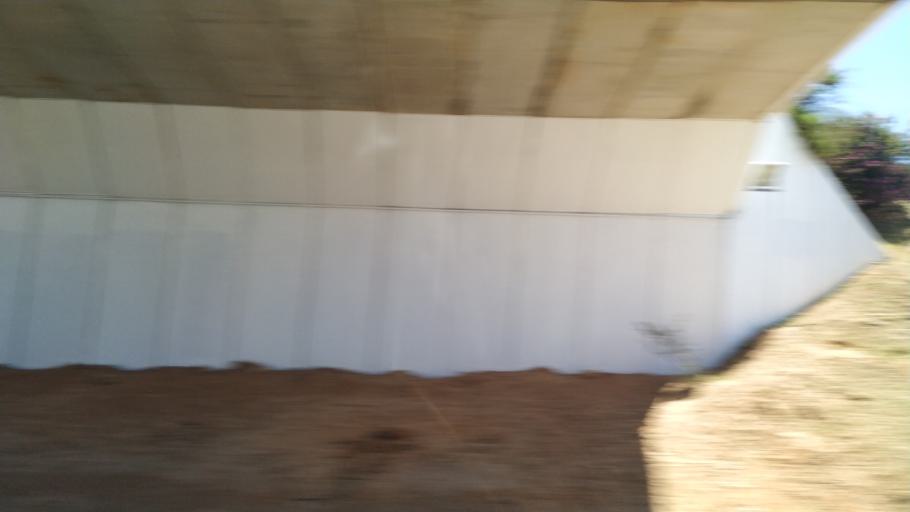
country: ES
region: Balearic Islands
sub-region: Illes Balears
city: Ibiza
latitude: 38.8822
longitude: 1.3834
